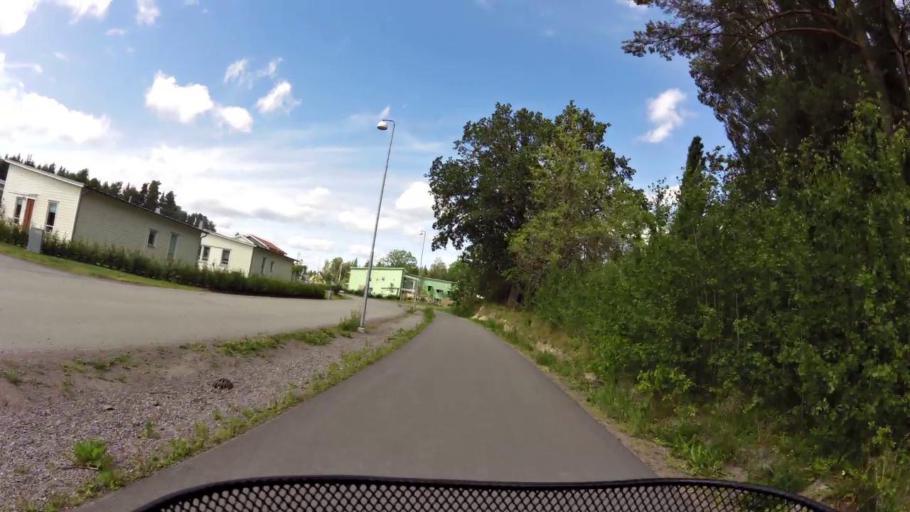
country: SE
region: OEstergoetland
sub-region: Linkopings Kommun
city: Ekangen
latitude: 58.4720
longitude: 15.6422
